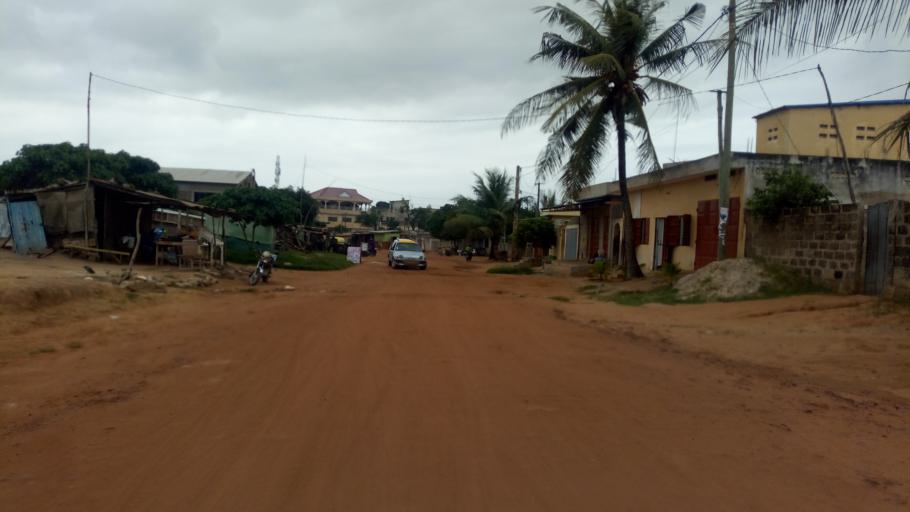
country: TG
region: Maritime
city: Lome
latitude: 6.1730
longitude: 1.1759
